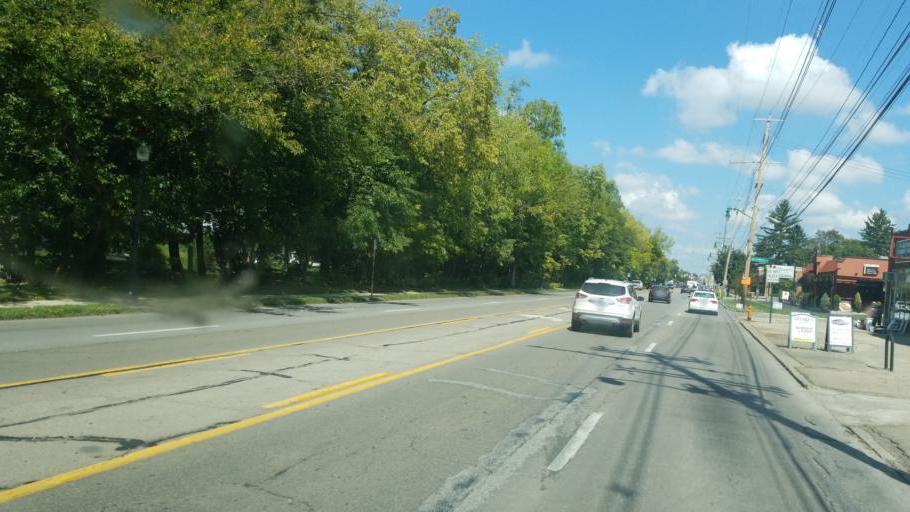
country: US
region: Ohio
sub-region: Franklin County
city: Worthington
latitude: 40.0593
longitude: -83.0196
